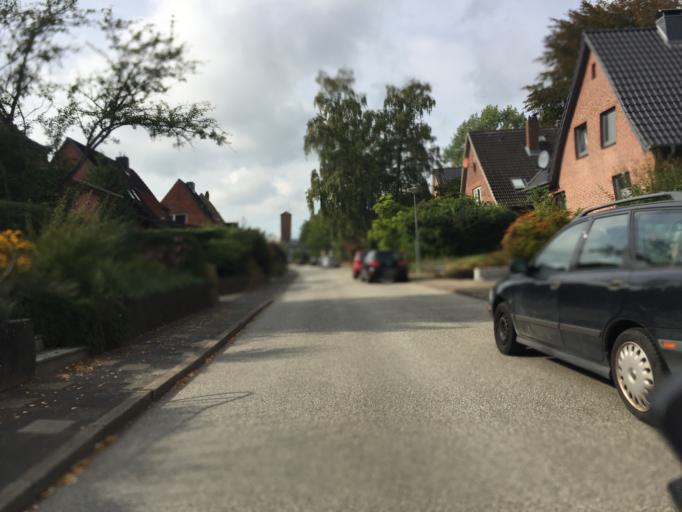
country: DE
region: Schleswig-Holstein
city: Itzehoe
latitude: 53.9270
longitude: 9.5341
